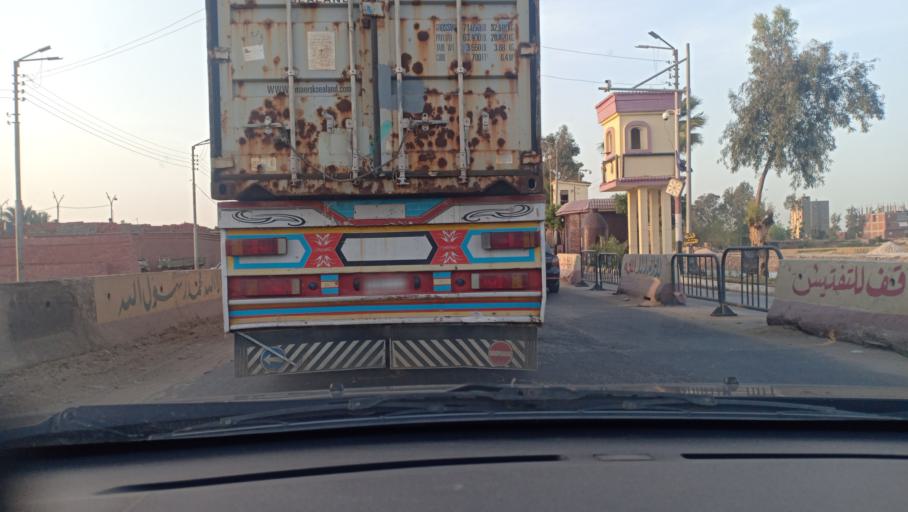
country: EG
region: Muhafazat al Gharbiyah
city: Zifta
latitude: 30.6065
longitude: 31.2752
